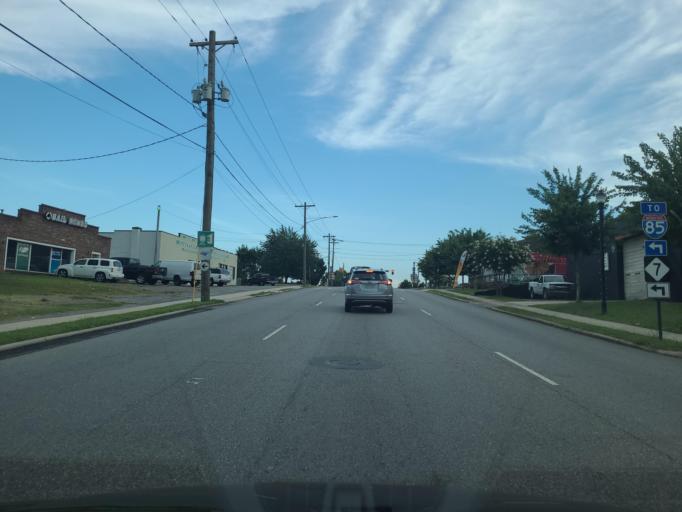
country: US
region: North Carolina
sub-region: Gaston County
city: Gastonia
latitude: 35.2665
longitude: -81.1874
